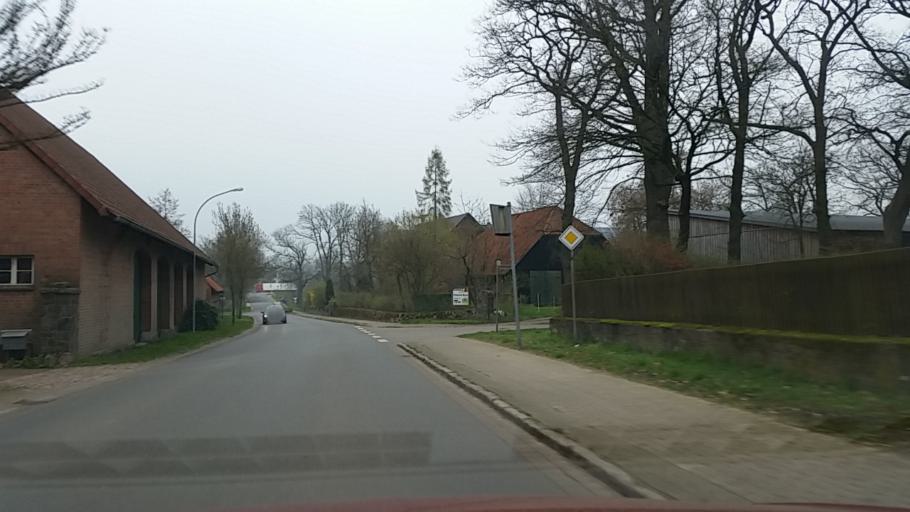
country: DE
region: Lower Saxony
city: Suderburg
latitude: 52.9512
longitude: 10.4830
